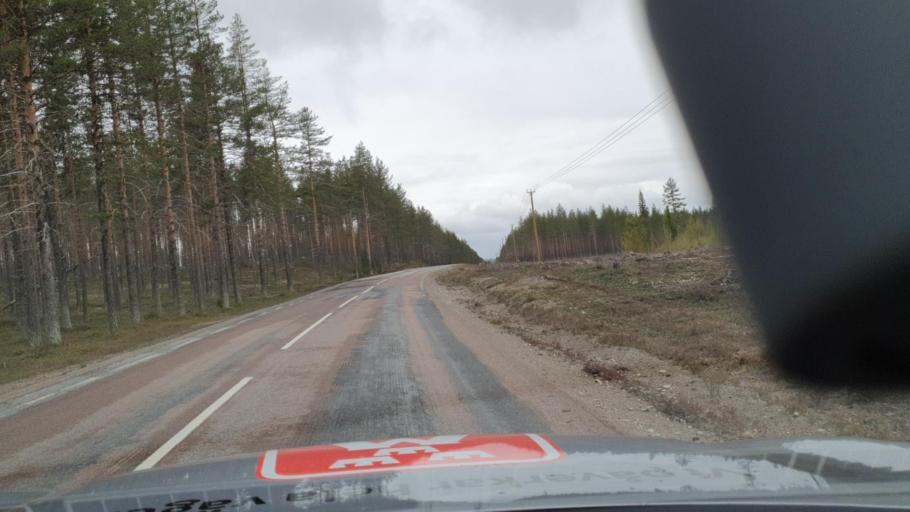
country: SE
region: Vaesternorrland
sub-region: Solleftea Kommun
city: Solleftea
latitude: 63.6128
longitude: 17.5064
